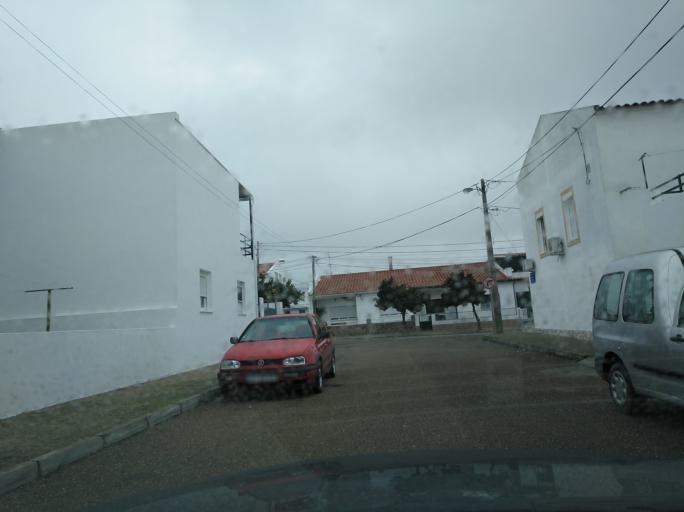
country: PT
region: Portalegre
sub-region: Campo Maior
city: Campo Maior
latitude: 39.0205
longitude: -7.0634
